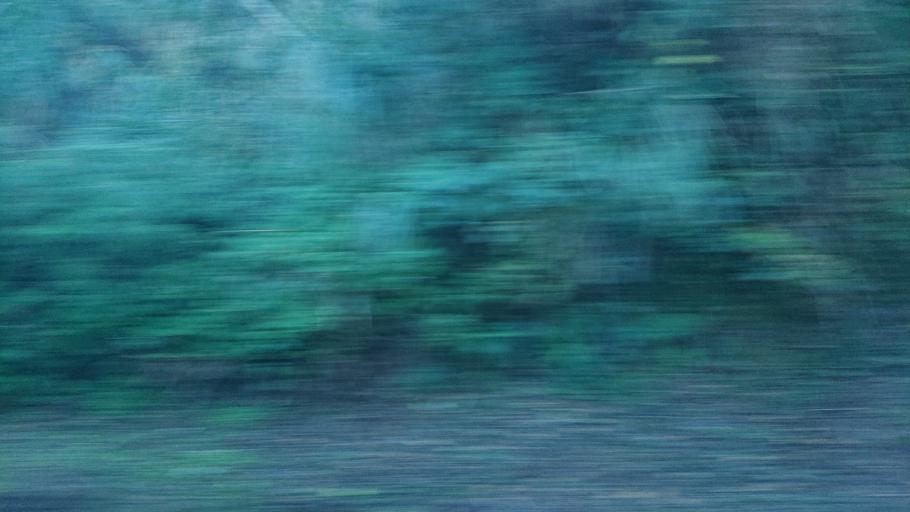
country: TW
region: Taiwan
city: Lugu
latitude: 23.4829
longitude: 120.8314
